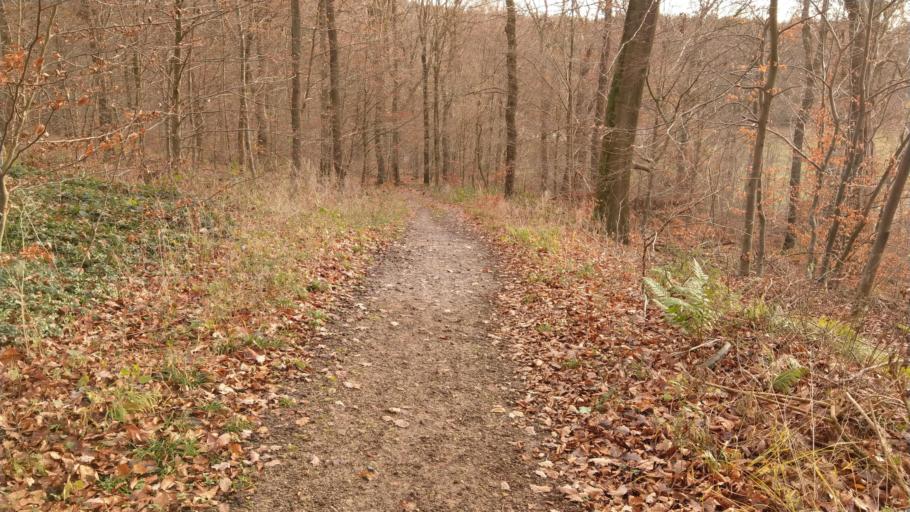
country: DE
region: North Rhine-Westphalia
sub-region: Regierungsbezirk Koln
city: Aachen
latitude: 50.7382
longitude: 6.0577
